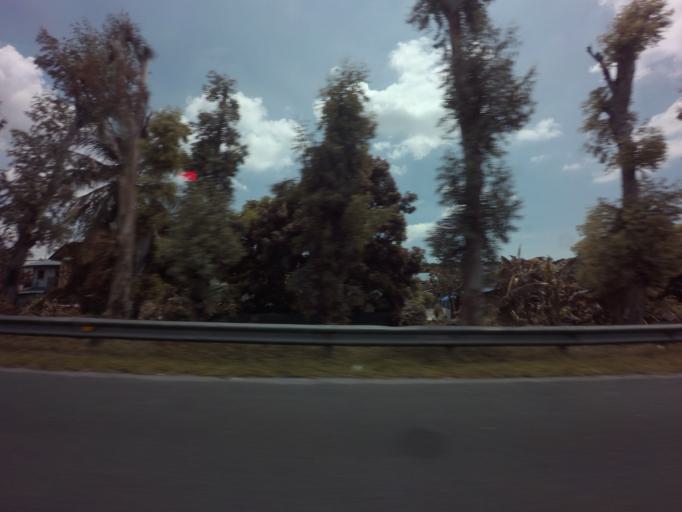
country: PH
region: Calabarzon
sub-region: Province of Laguna
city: San Pedro
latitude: 14.4053
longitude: 121.0402
